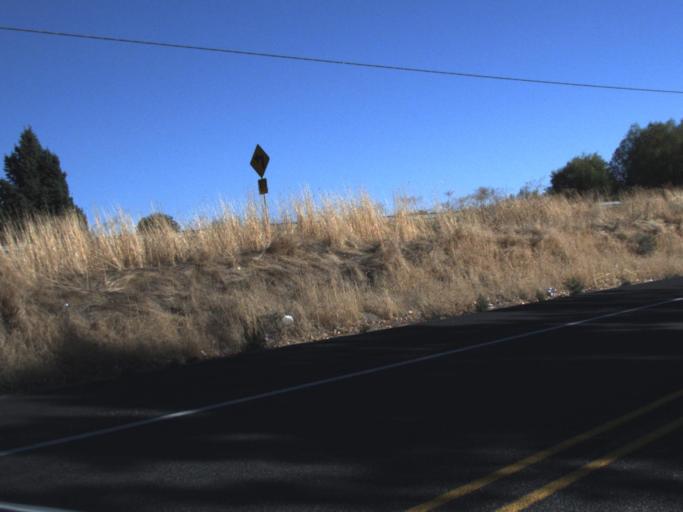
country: US
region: Washington
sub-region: Franklin County
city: Pasco
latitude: 46.1929
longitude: -119.0759
